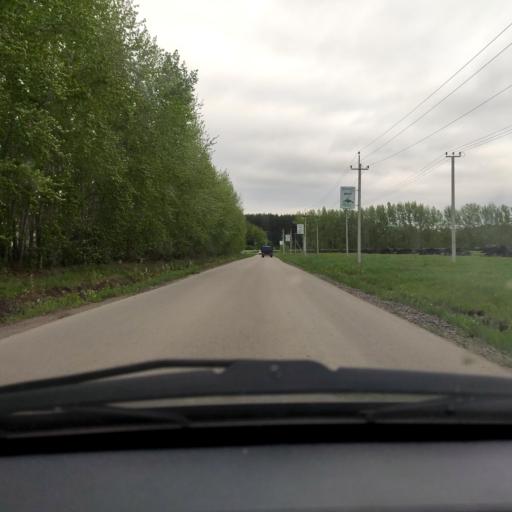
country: RU
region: Bashkortostan
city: Kabakovo
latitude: 54.6156
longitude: 56.1587
